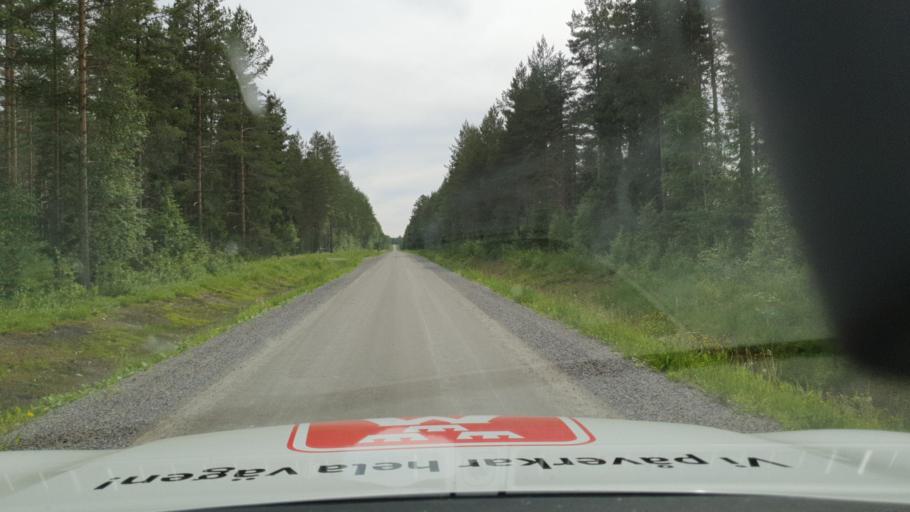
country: SE
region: Vaesterbotten
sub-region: Skelleftea Kommun
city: Burea
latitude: 64.4568
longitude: 21.0305
